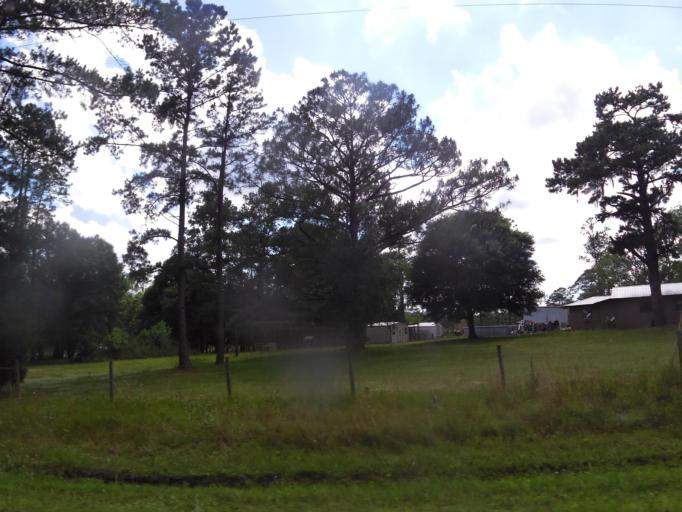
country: US
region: Florida
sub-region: Clay County
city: Asbury Lake
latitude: 29.9076
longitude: -81.8767
